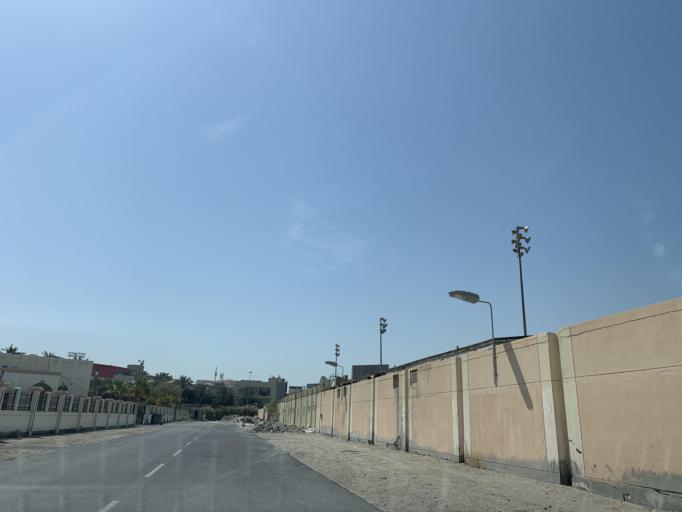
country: BH
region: Muharraq
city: Al Muharraq
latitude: 26.2644
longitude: 50.6141
